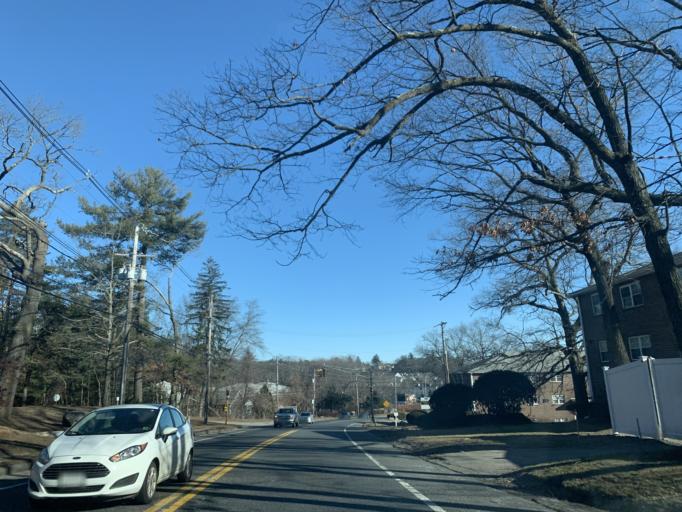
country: US
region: Massachusetts
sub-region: Middlesex County
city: Marlborough
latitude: 42.3494
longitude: -71.5208
